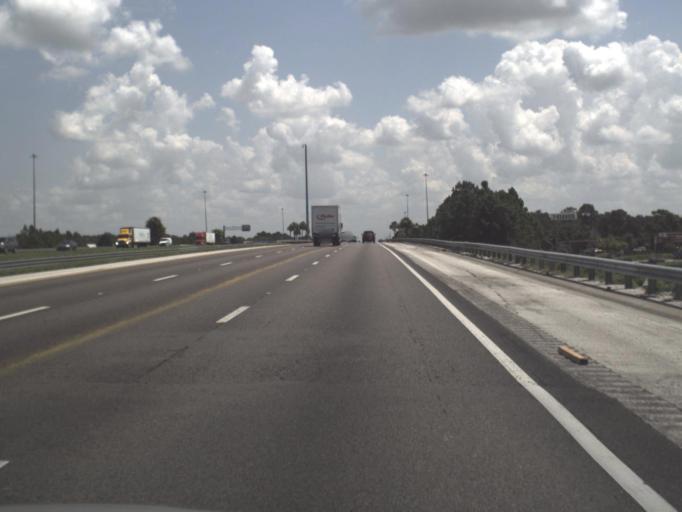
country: US
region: Florida
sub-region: Hillsborough County
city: Dover
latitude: 28.0222
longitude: -82.2476
